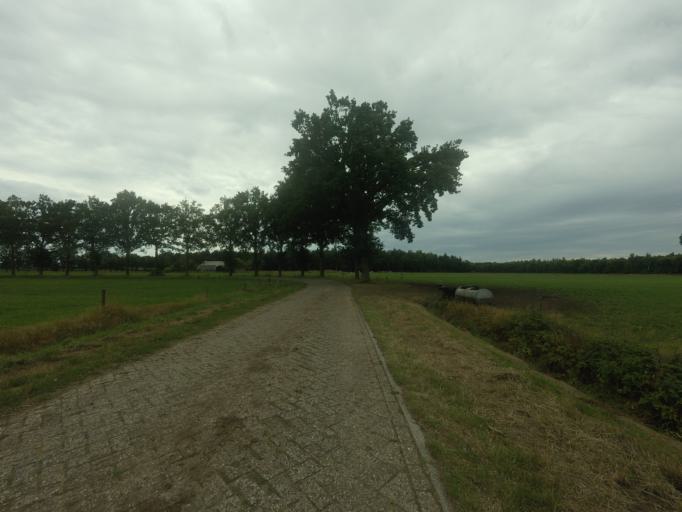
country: NL
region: Overijssel
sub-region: Gemeente Raalte
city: Raalte
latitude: 52.3500
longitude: 6.3251
